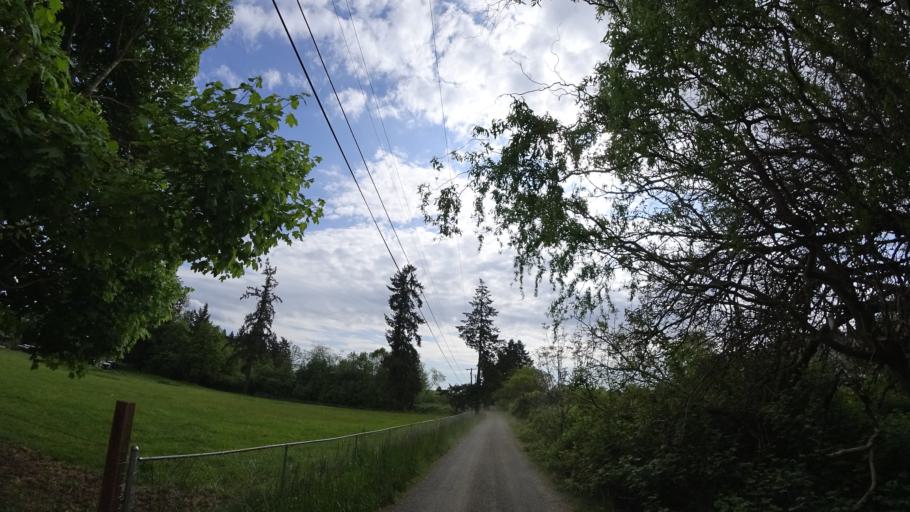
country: US
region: Oregon
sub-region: Washington County
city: Hillsboro
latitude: 45.4904
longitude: -122.9608
